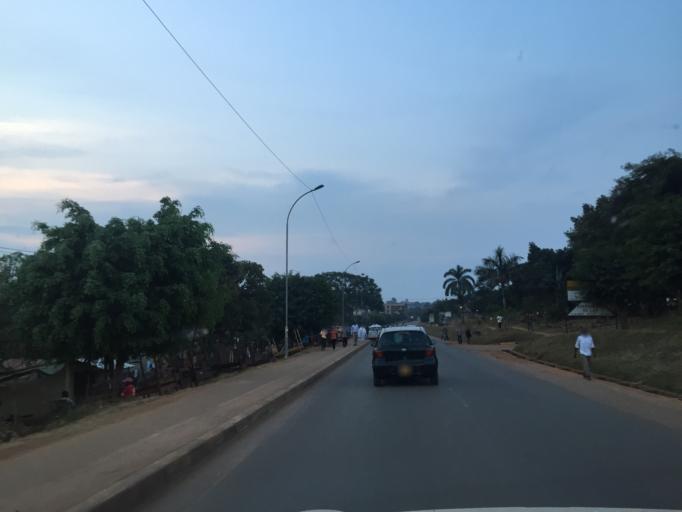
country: UG
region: Central Region
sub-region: Kampala District
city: Kampala
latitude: 0.2614
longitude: 32.6258
